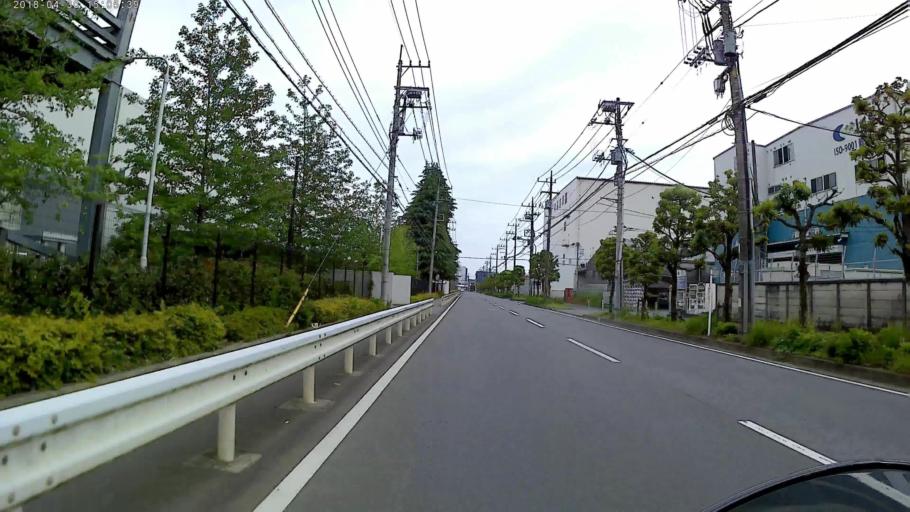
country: JP
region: Kanagawa
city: Zama
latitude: 35.5585
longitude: 139.3418
